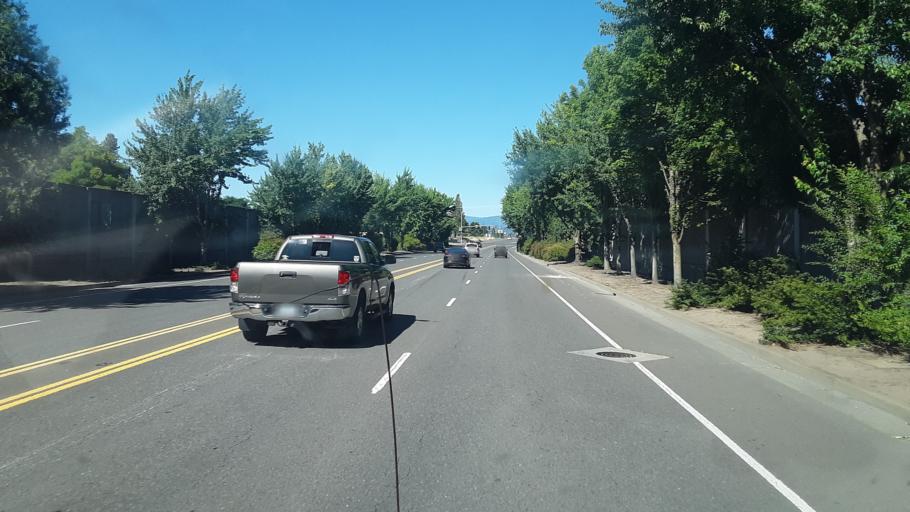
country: US
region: Oregon
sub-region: Josephine County
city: Grants Pass
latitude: 42.4261
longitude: -123.3251
